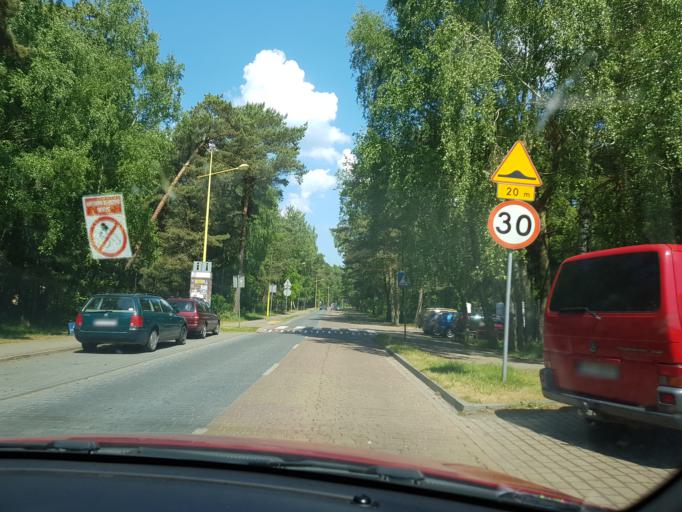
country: PL
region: West Pomeranian Voivodeship
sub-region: Powiat gryficki
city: Karnice
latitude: 54.0976
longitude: 15.0998
